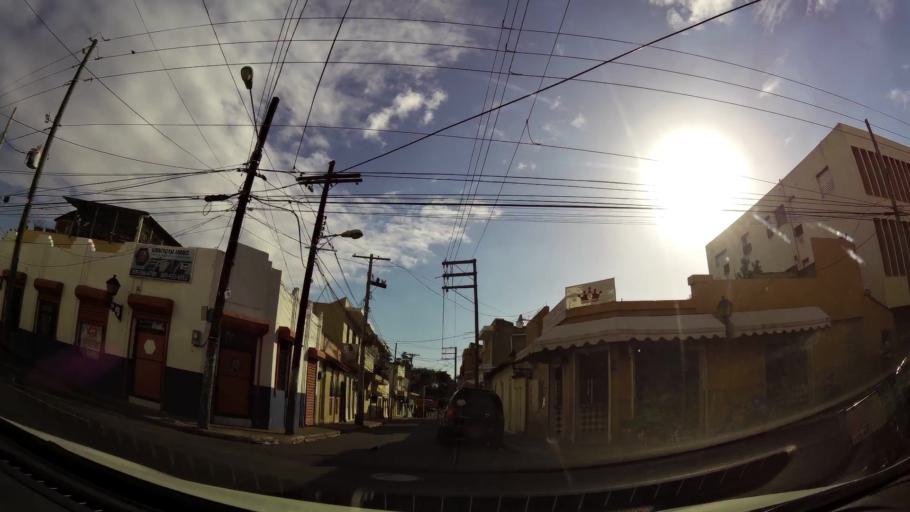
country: DO
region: Nacional
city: San Carlos
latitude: 18.4769
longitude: -69.8872
